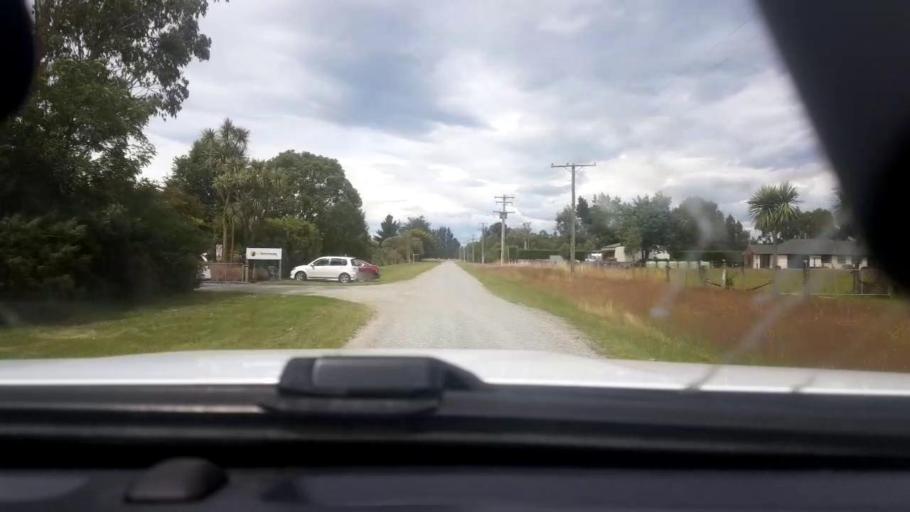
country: NZ
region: Canterbury
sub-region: Timaru District
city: Pleasant Point
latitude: -44.1408
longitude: 171.2904
